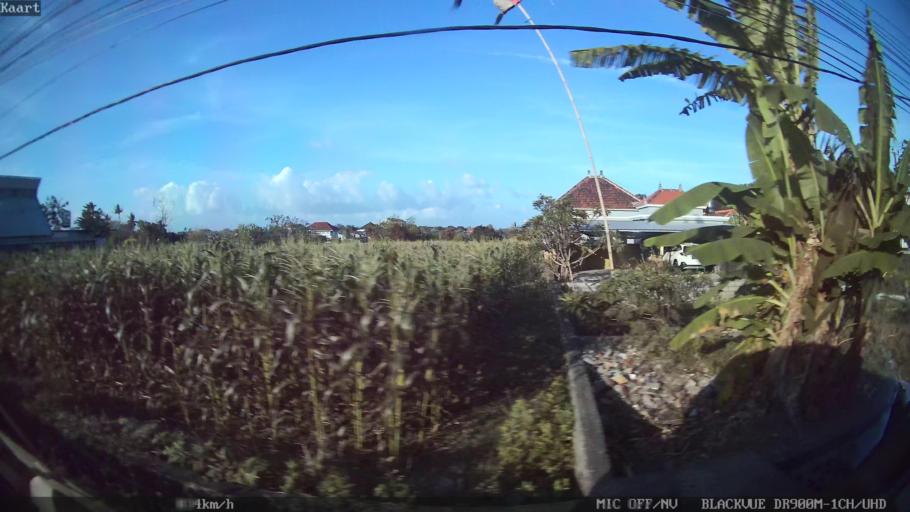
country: ID
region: Bali
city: Dajan Tangluk
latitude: -8.6530
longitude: 115.2514
